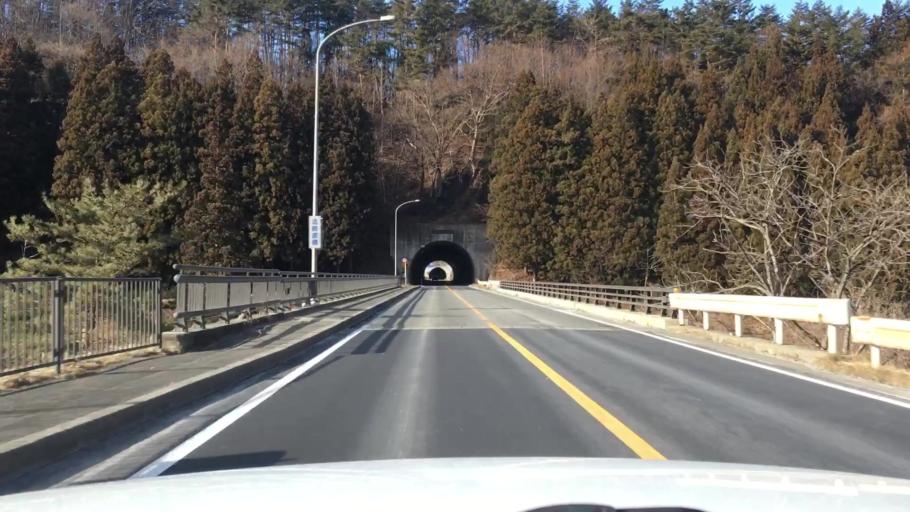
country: JP
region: Iwate
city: Tono
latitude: 39.6313
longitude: 141.6055
